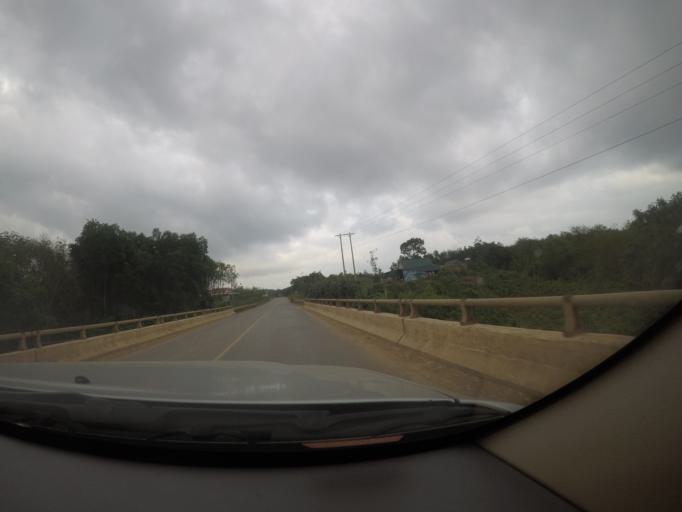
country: VN
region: Quang Tri
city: Ho Xa
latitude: 17.0172
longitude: 106.9095
